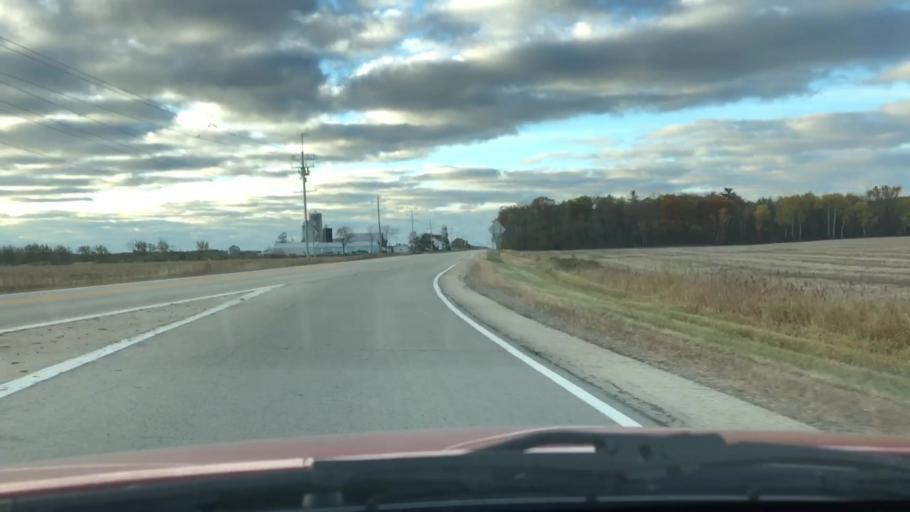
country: US
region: Wisconsin
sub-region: Outagamie County
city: Seymour
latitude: 44.4977
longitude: -88.2913
